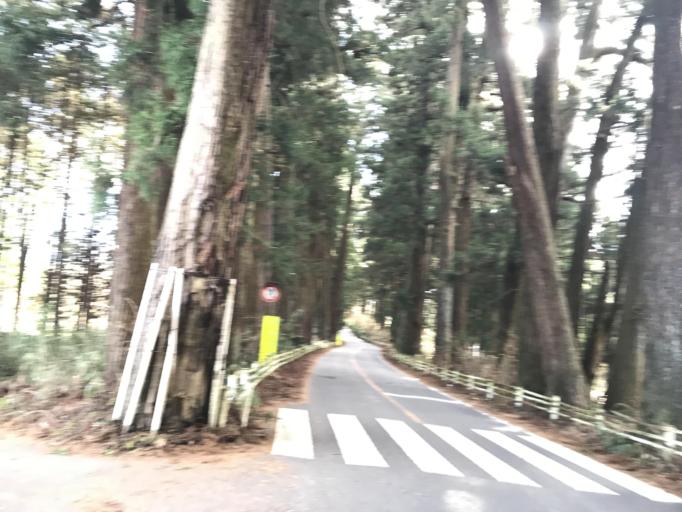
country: JP
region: Tochigi
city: Imaichi
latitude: 36.6898
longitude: 139.7173
